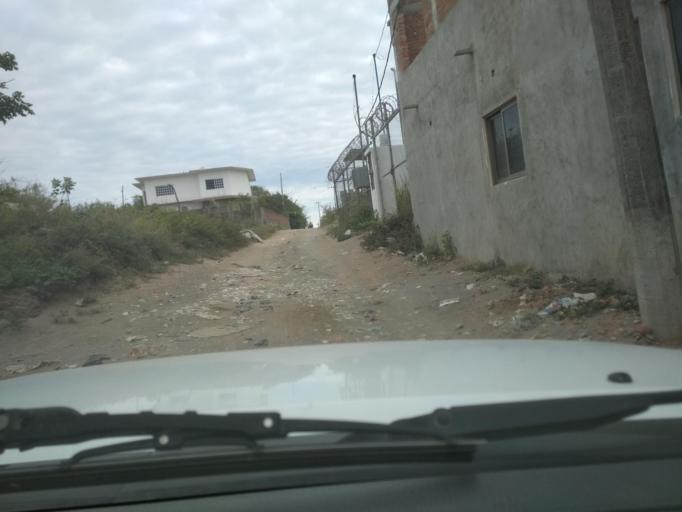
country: MX
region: Veracruz
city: Anton Lizardo
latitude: 19.0545
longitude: -95.9930
